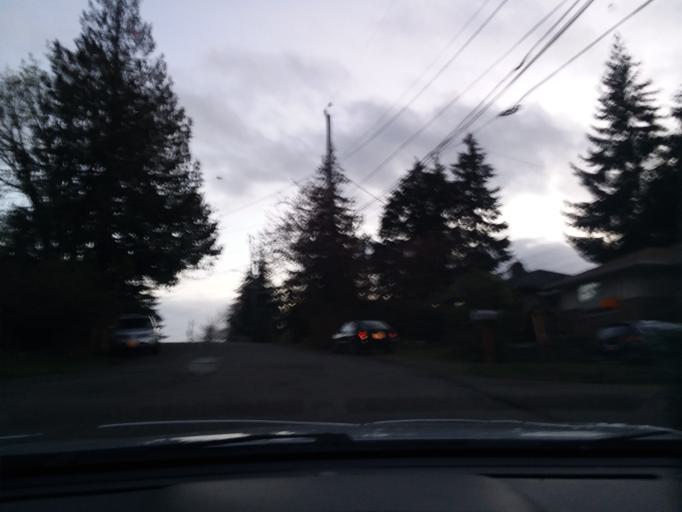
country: US
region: Washington
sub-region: Snohomish County
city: Mountlake Terrace
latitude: 47.7656
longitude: -122.3162
